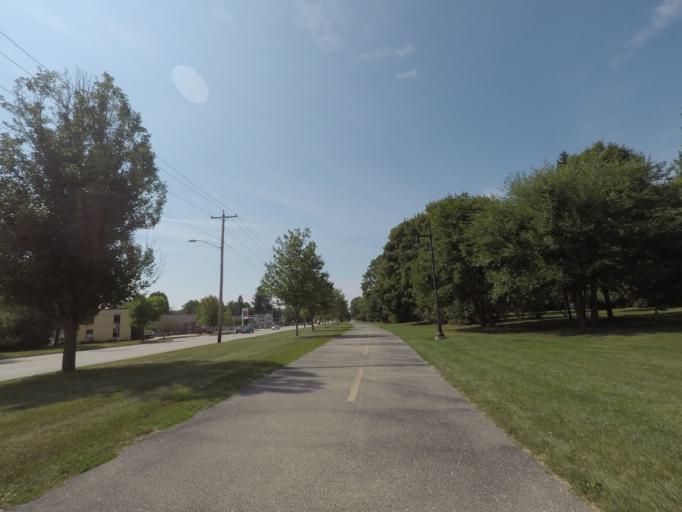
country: US
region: Wisconsin
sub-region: Jefferson County
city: Fort Atkinson
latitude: 42.9245
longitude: -88.8425
